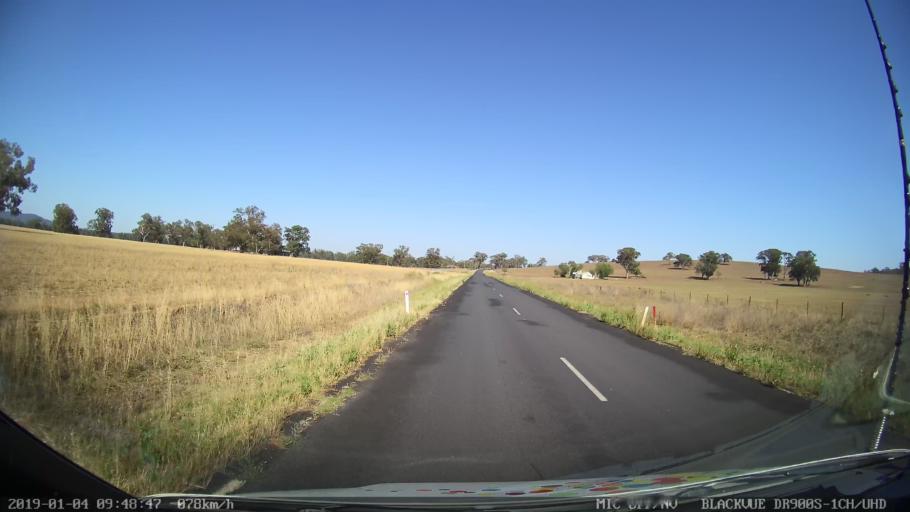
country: AU
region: New South Wales
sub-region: Cabonne
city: Canowindra
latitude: -33.5967
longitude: 148.4282
